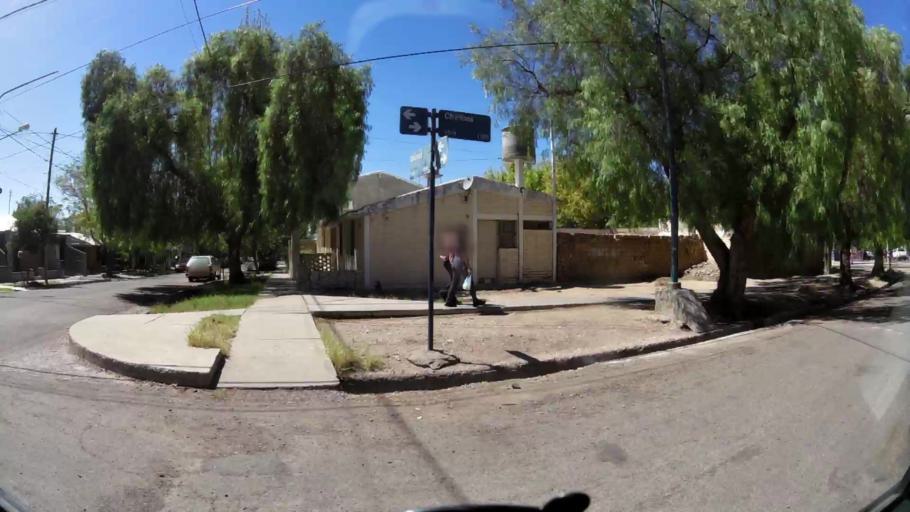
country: AR
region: Mendoza
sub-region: Departamento de Godoy Cruz
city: Godoy Cruz
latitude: -32.9354
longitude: -68.8745
